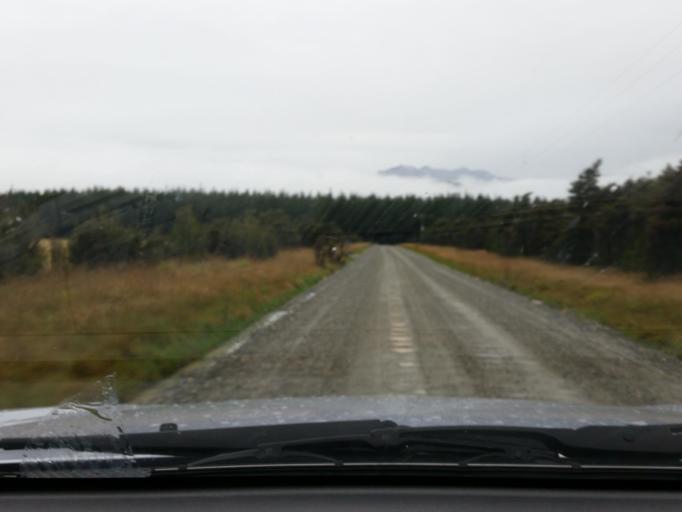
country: NZ
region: Southland
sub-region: Southland District
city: Te Anau
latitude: -45.7783
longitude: 167.5890
